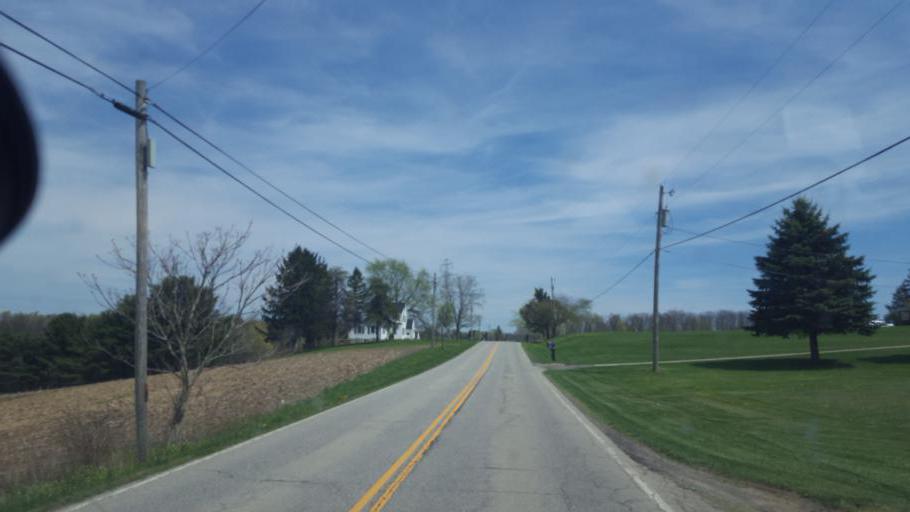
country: US
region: Ohio
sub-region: Richland County
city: Lexington
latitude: 40.6813
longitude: -82.5459
